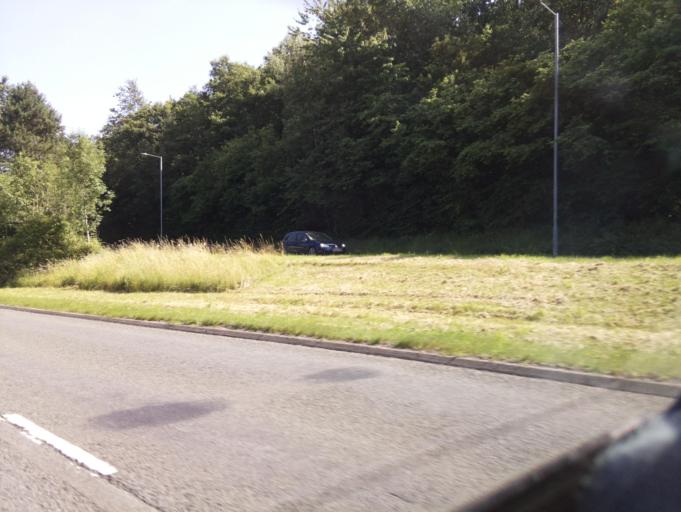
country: GB
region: England
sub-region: Worcestershire
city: Redditch
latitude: 52.2986
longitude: -1.9590
